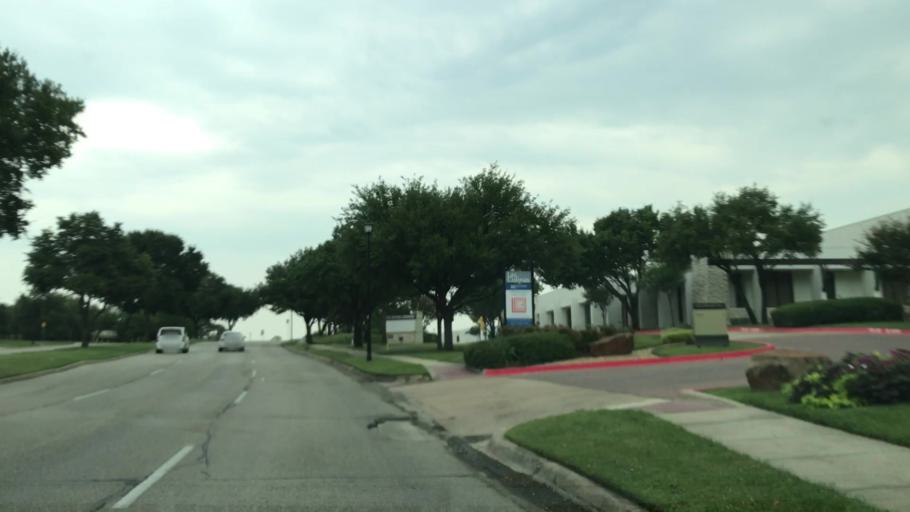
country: US
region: Texas
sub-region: Dallas County
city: Irving
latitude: 32.8803
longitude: -96.9744
